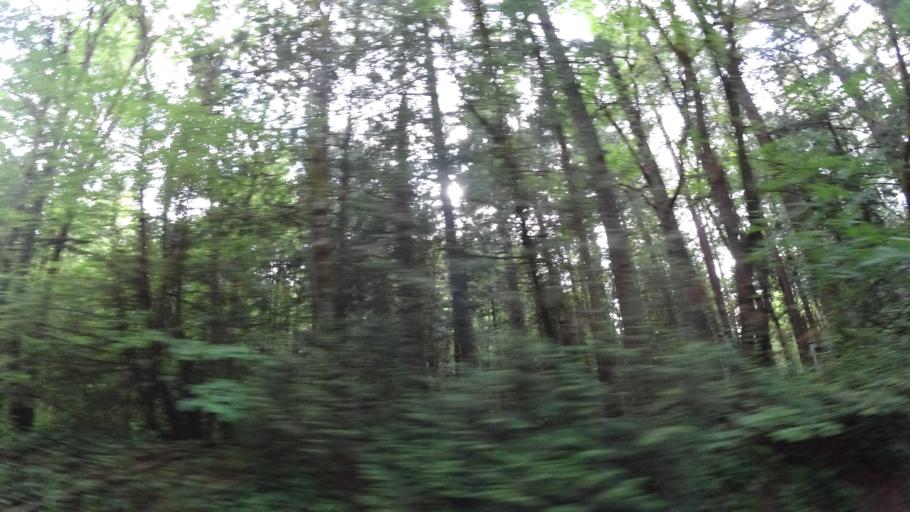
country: US
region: Oregon
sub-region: Washington County
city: Garden Home-Whitford
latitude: 45.4716
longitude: -122.7231
